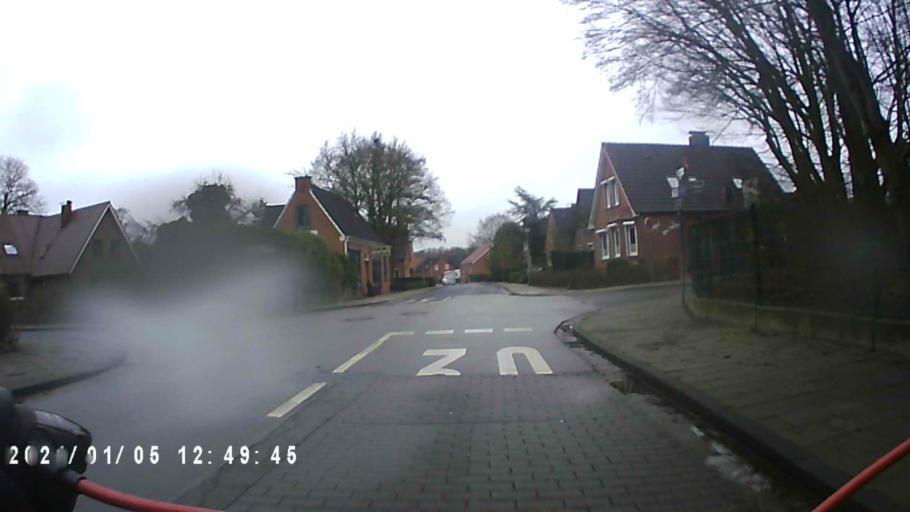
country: DE
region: Lower Saxony
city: Leer
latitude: 53.2354
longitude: 7.4973
